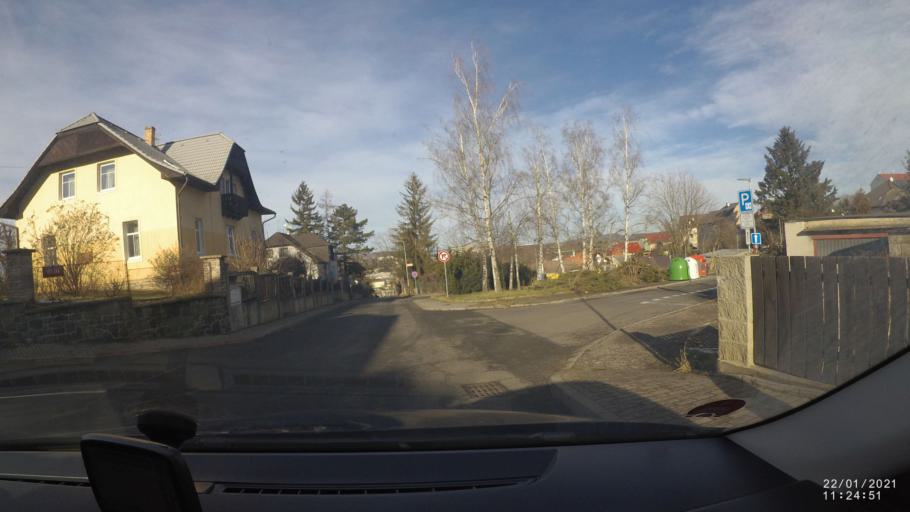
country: CZ
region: Central Bohemia
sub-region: Okres Beroun
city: Horovice
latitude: 49.8348
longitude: 13.9000
